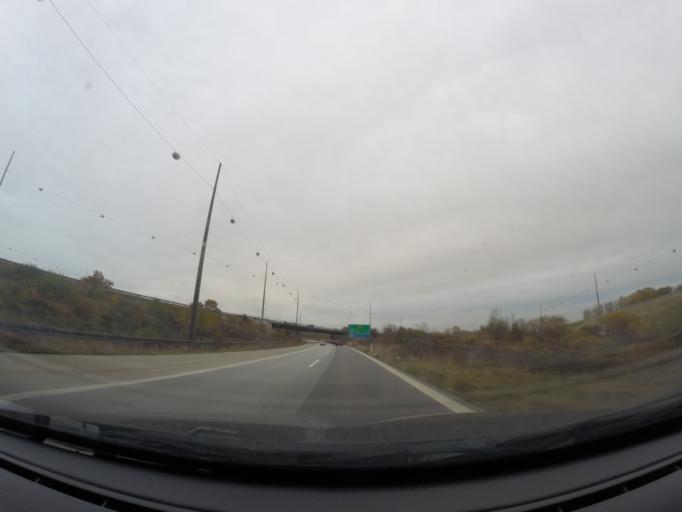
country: DK
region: Capital Region
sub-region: Ishoj Kommune
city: Ishoj
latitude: 55.6354
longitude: 12.3349
